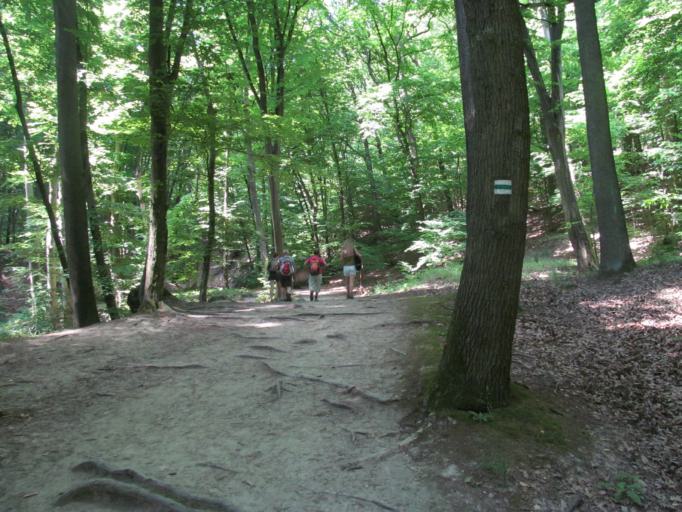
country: HU
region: Komarom-Esztergom
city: Pilismarot
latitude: 47.7442
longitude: 18.8993
